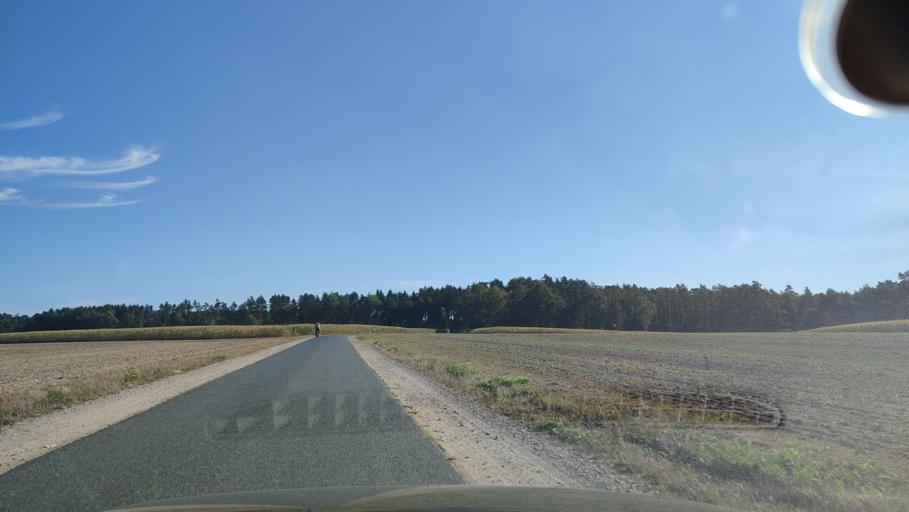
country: DE
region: Lower Saxony
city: Bomlitz
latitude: 52.8867
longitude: 9.6569
